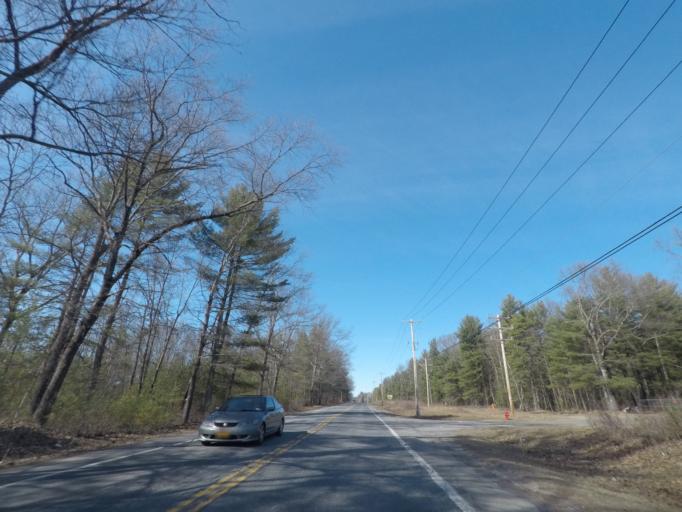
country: US
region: New York
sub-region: Saratoga County
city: Milton
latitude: 43.0544
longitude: -73.8506
